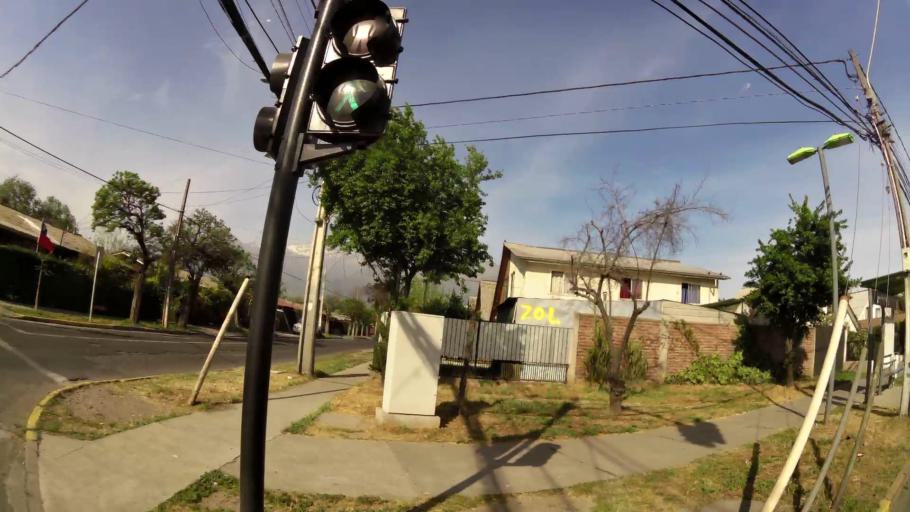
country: CL
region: Santiago Metropolitan
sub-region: Provincia de Santiago
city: La Pintana
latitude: -33.5303
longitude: -70.5901
